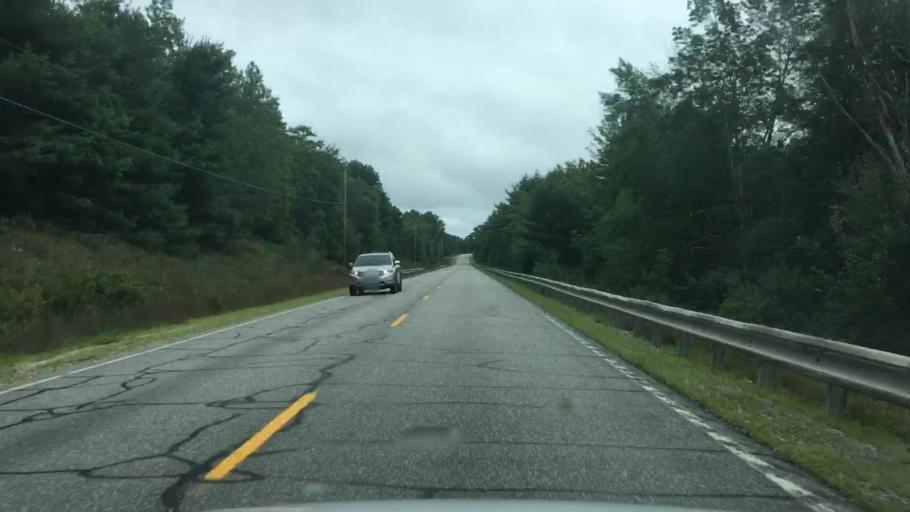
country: US
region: Maine
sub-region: Oxford County
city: Brownfield
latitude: 43.9181
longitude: -70.8566
